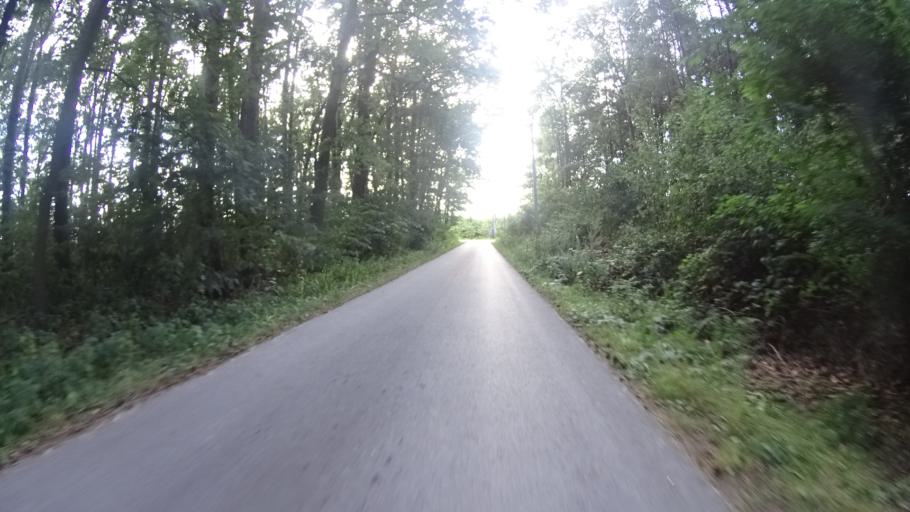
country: PL
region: Masovian Voivodeship
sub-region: Powiat bialobrzeski
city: Wysmierzyce
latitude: 51.6757
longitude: 20.8011
